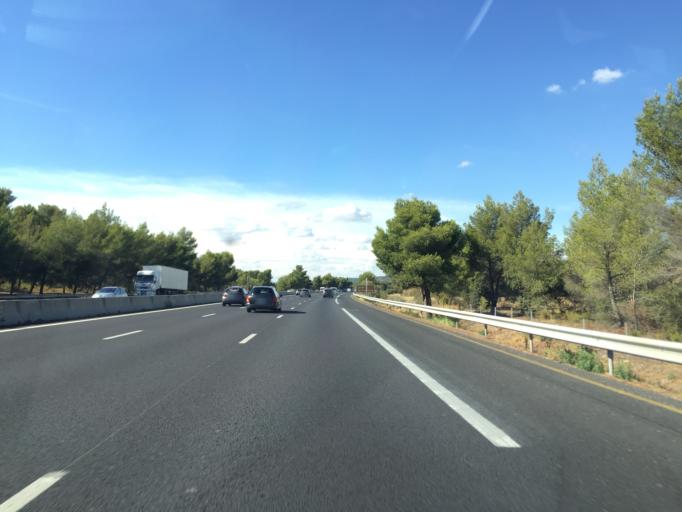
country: FR
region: Provence-Alpes-Cote d'Azur
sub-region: Departement des Bouches-du-Rhone
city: Lancon-Provence
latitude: 43.6022
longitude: 5.1539
